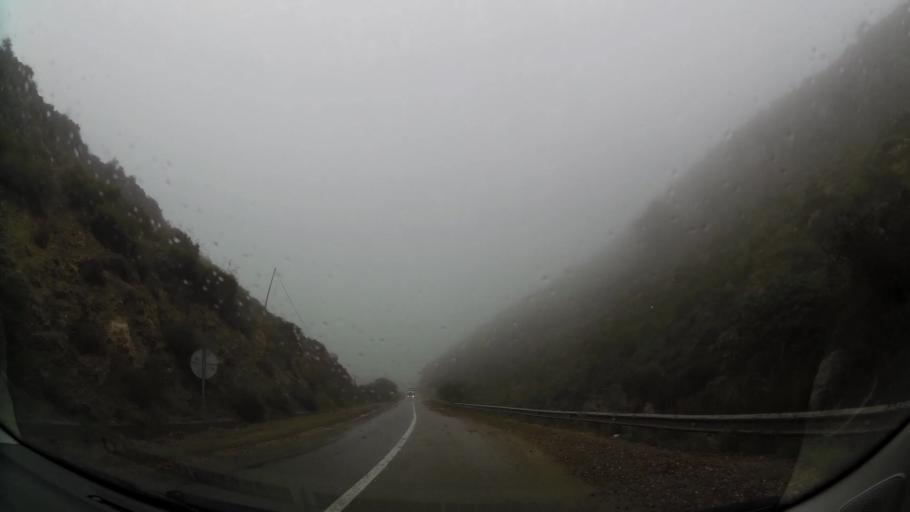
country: MA
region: Taza-Al Hoceima-Taounate
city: Tirhanimine
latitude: 35.2303
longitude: -3.9666
